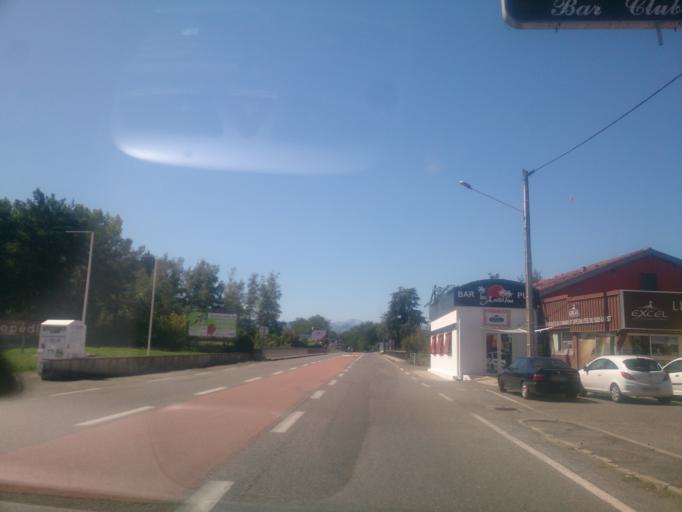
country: FR
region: Midi-Pyrenees
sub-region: Departement des Hautes-Pyrenees
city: Odos
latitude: 43.2096
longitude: 0.0464
